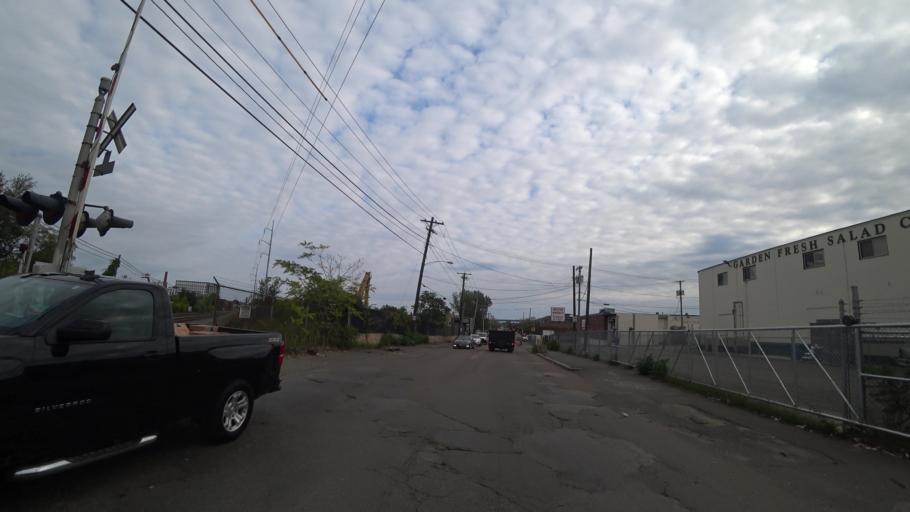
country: US
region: Massachusetts
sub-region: Middlesex County
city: Everett
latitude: 42.3983
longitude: -71.0481
